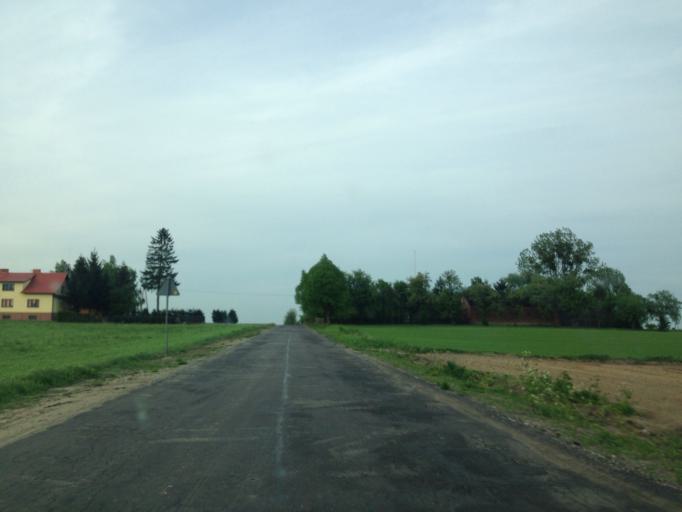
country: PL
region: Kujawsko-Pomorskie
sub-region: Powiat brodnicki
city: Bobrowo
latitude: 53.2788
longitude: 19.3203
